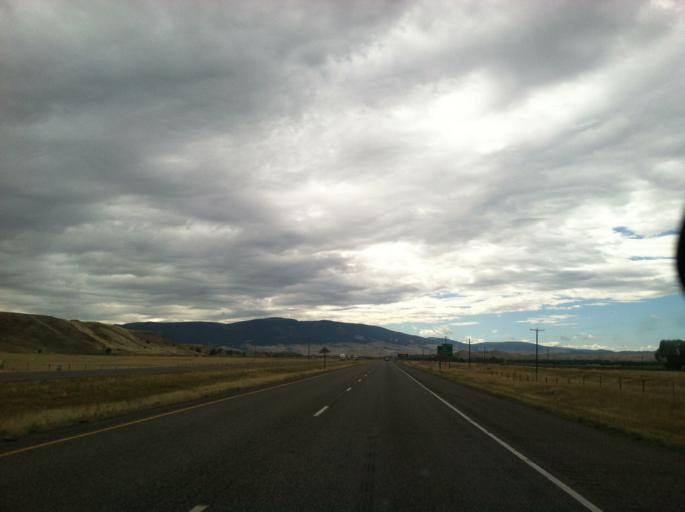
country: US
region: Montana
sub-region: Park County
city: Livingston
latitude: 45.6961
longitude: -110.4821
